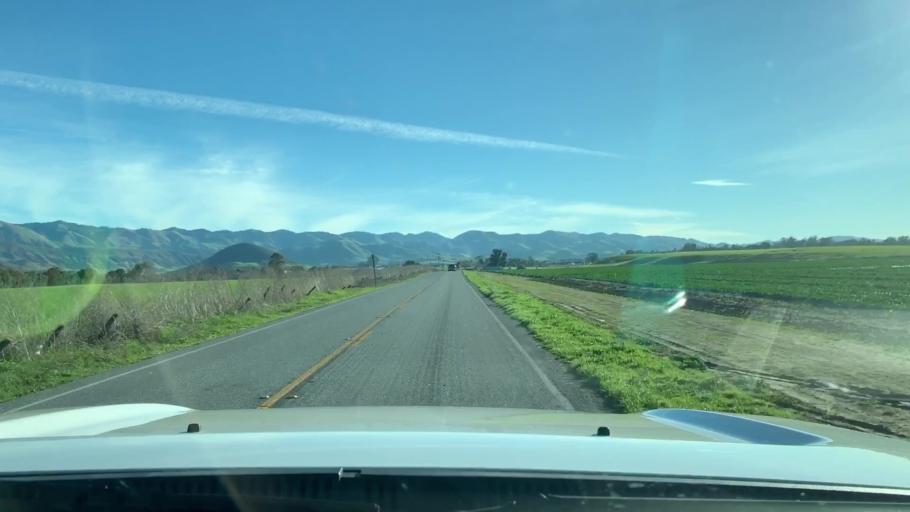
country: US
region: California
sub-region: San Luis Obispo County
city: San Luis Obispo
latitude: 35.2359
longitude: -120.6661
